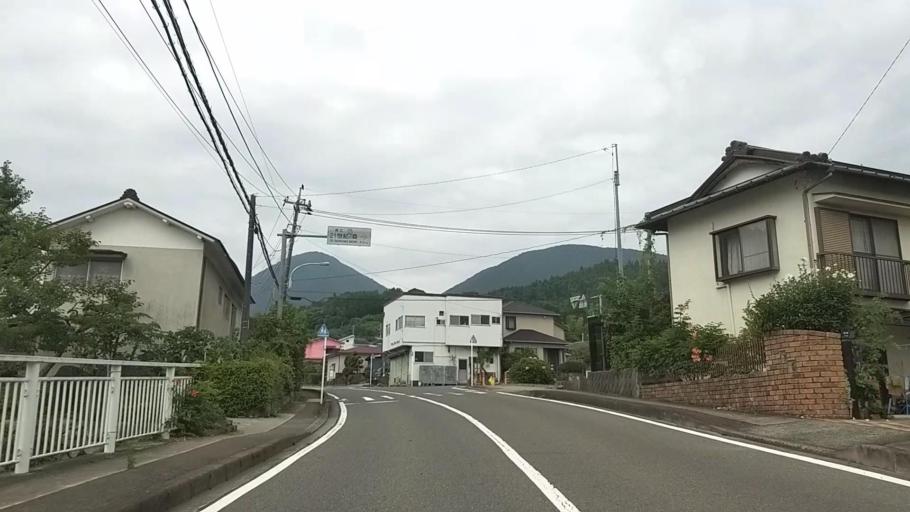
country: JP
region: Kanagawa
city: Odawara
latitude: 35.3314
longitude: 139.0715
